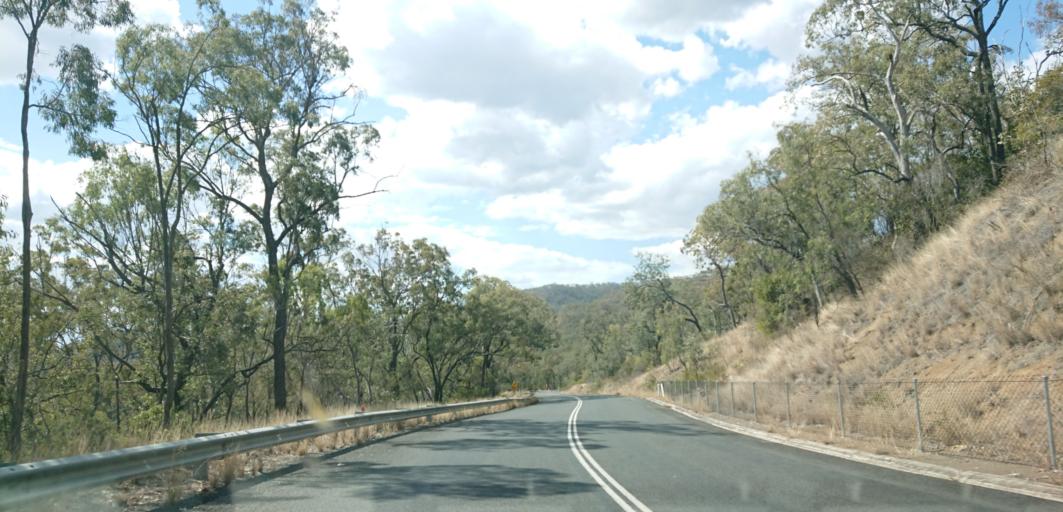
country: AU
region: Queensland
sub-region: Toowoomba
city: Top Camp
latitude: -27.8177
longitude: 152.1043
